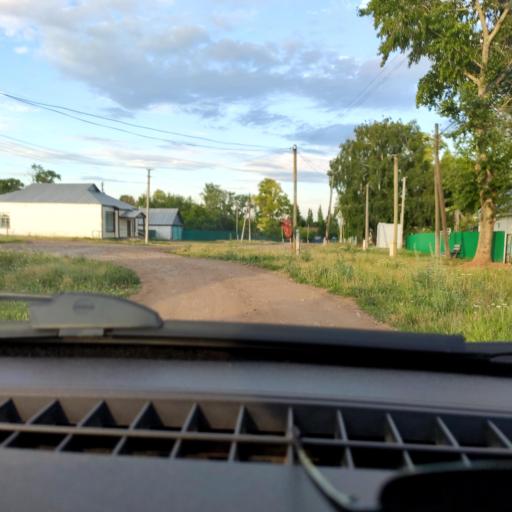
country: RU
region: Bashkortostan
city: Chishmy
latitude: 54.3742
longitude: 55.4204
